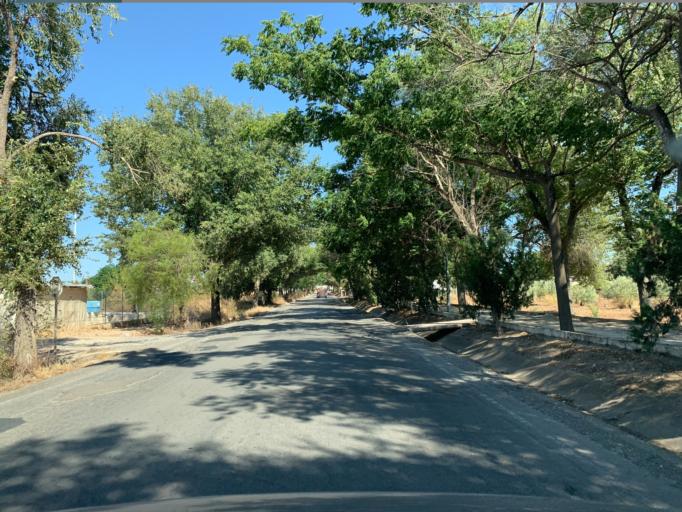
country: ES
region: Andalusia
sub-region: Provincia de Sevilla
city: Marinaleda
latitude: 37.3675
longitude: -4.9671
